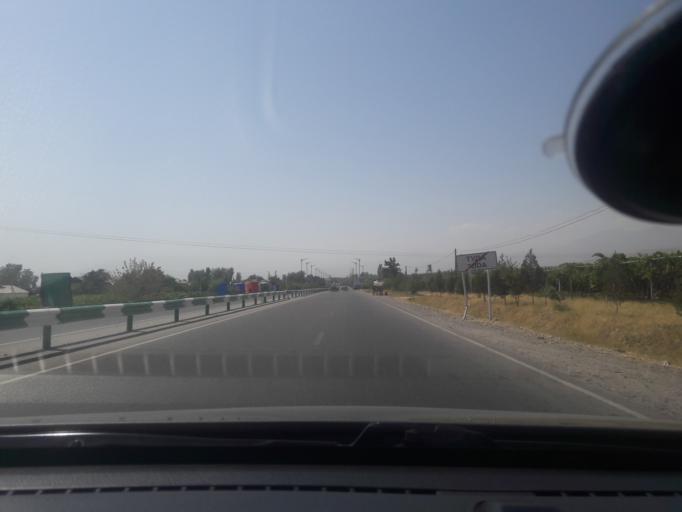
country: TJ
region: Republican Subordination
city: Hisor
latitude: 38.5602
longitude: 68.4525
